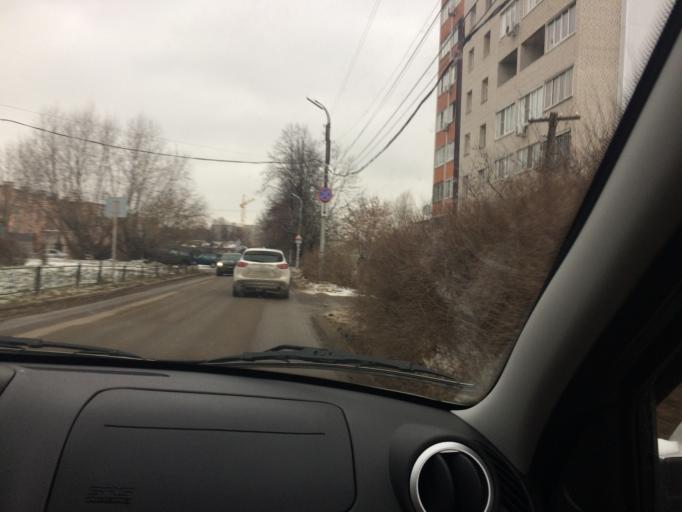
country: RU
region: Rjazan
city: Ryazan'
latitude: 54.6184
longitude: 39.7138
